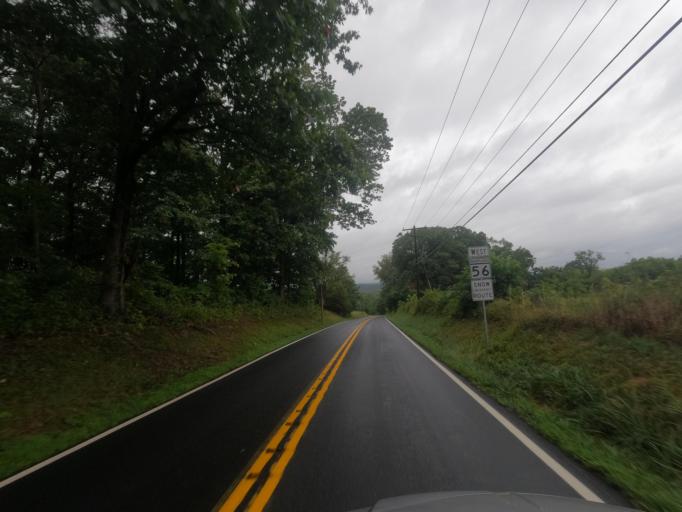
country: US
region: West Virginia
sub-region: Berkeley County
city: Martinsburg
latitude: 39.6182
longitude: -78.0029
